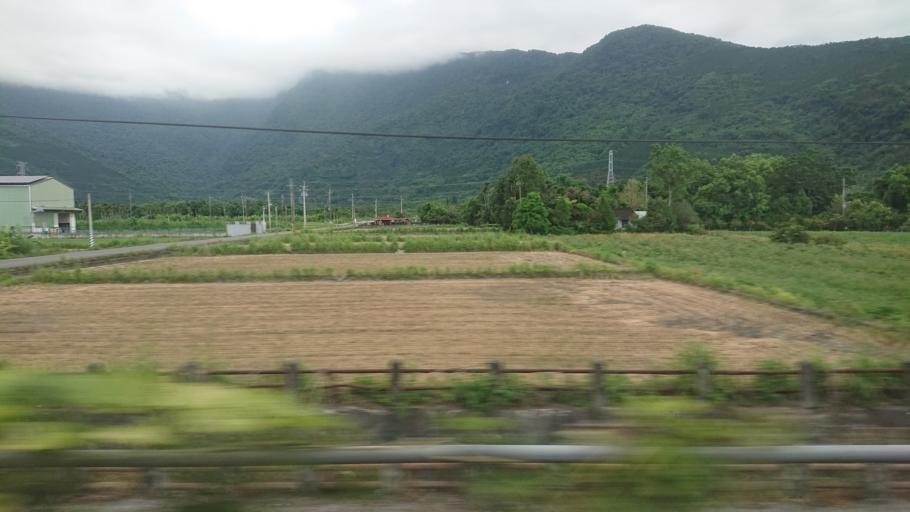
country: TW
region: Taiwan
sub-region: Hualien
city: Hualian
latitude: 23.7541
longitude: 121.4507
